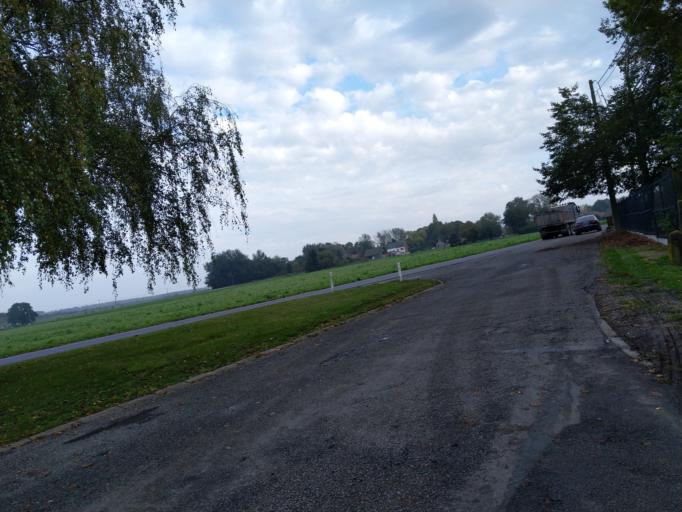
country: BE
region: Wallonia
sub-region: Province du Hainaut
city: Brugelette
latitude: 50.6105
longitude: 3.8325
